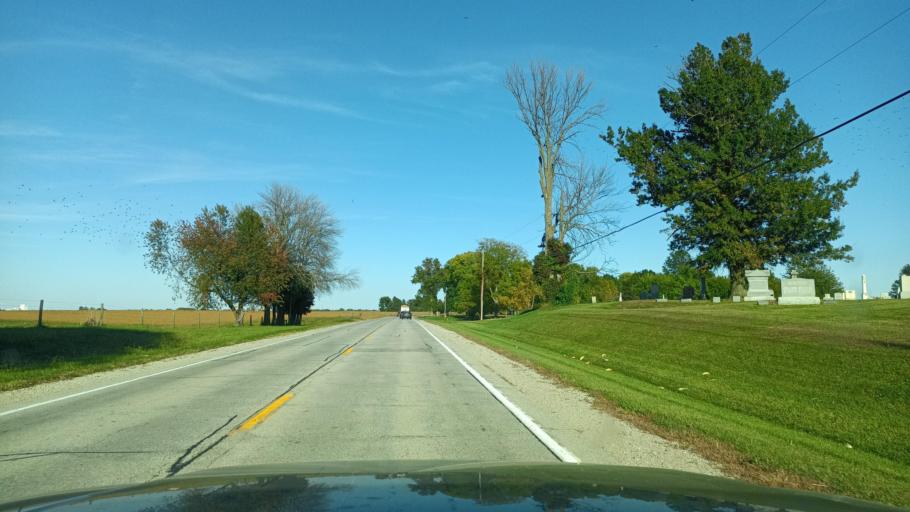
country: US
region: Illinois
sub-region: De Witt County
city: Farmer City
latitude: 40.2302
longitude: -88.6796
